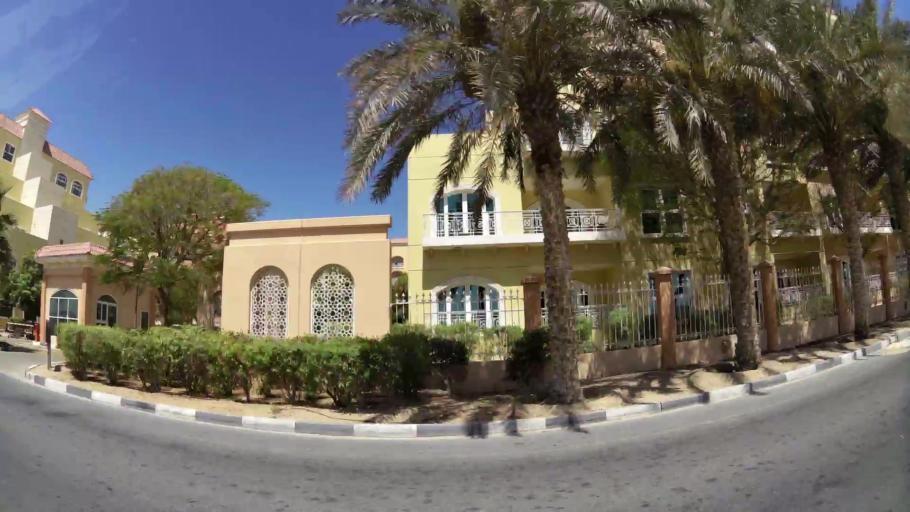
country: AE
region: Dubai
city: Dubai
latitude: 24.9882
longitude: 55.2041
